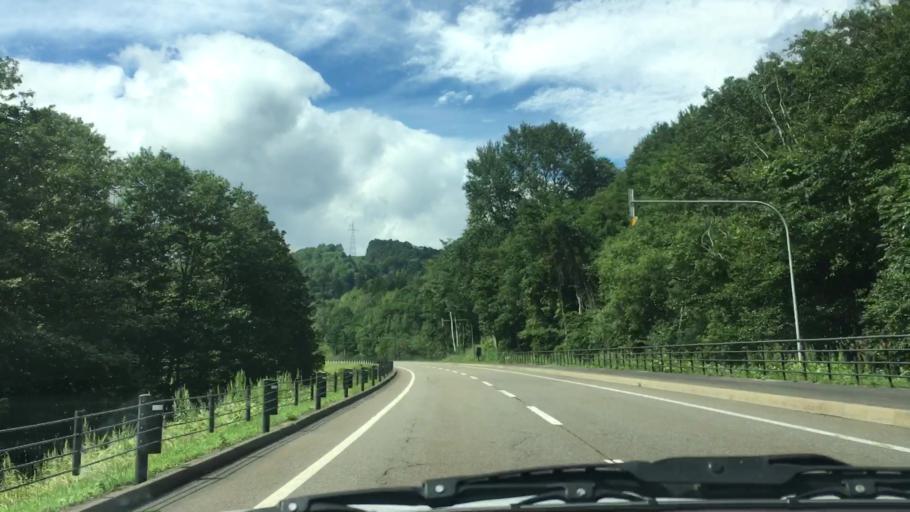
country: JP
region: Hokkaido
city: Otofuke
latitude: 43.3674
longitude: 143.2332
